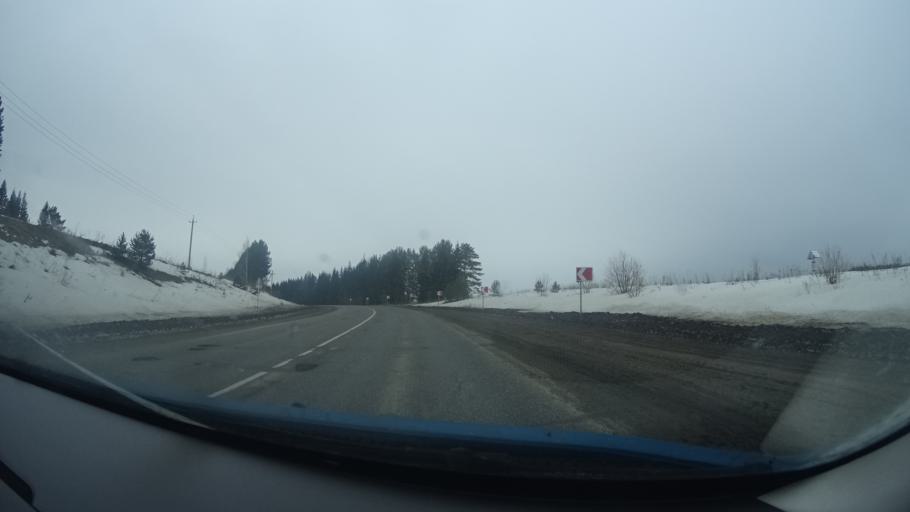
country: RU
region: Perm
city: Osa
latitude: 57.3154
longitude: 55.6236
